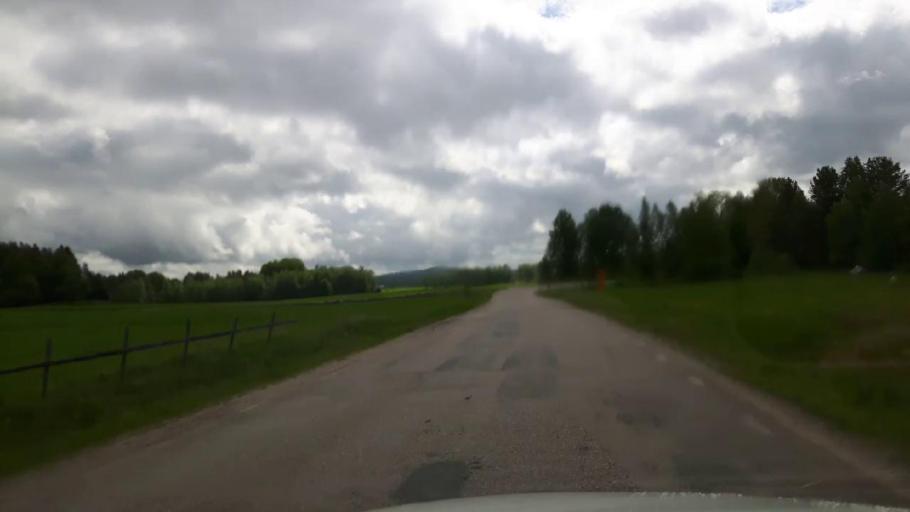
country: SE
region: Gaevleborg
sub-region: Ovanakers Kommun
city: Edsbyn
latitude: 61.3531
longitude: 15.9164
